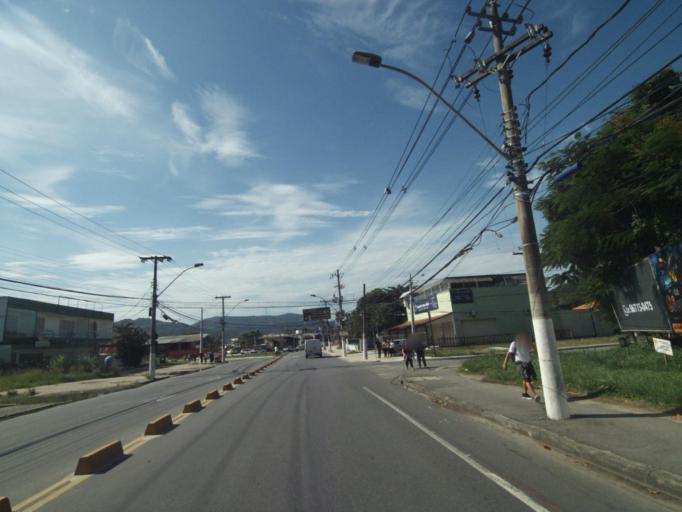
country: BR
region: Rio de Janeiro
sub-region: Niteroi
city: Niteroi
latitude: -22.9551
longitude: -43.0281
